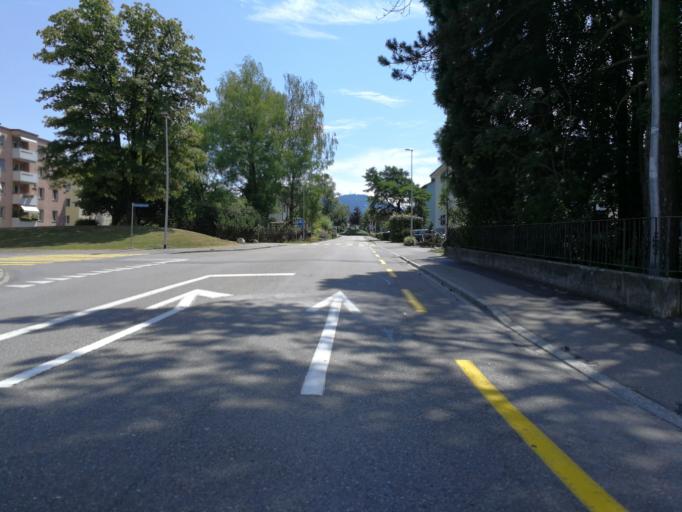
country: CH
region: Zurich
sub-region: Bezirk Hinwil
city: Wetzikon / Ober-Wetzikon
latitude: 47.3259
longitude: 8.8046
